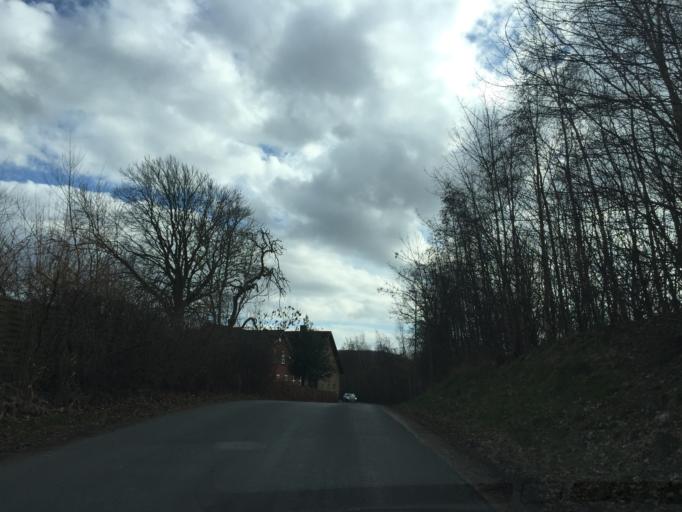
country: DK
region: South Denmark
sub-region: Svendborg Kommune
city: Svendborg
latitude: 55.1070
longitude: 10.5141
